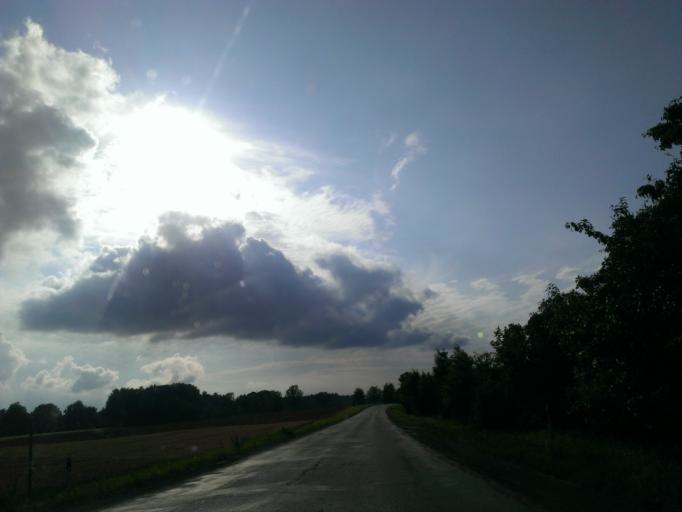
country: LV
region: Priekuli
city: Priekuli
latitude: 57.3098
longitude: 25.3456
